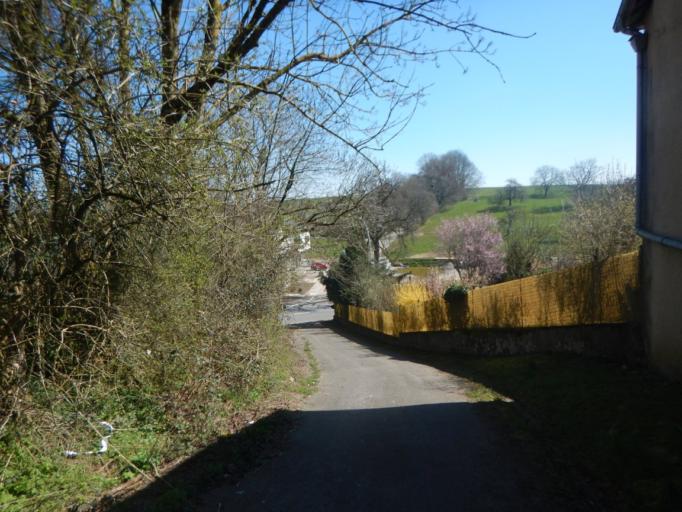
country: LU
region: Luxembourg
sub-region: Canton de Capellen
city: Garnich
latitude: 49.6017
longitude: 5.9472
